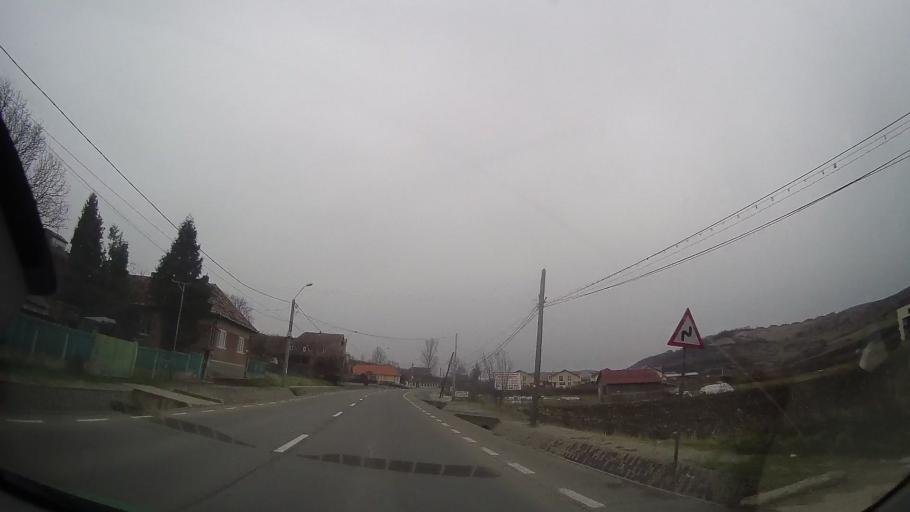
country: RO
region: Mures
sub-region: Comuna Ceausu de Campie
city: Ceausu de Campie
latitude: 46.6053
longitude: 24.5298
